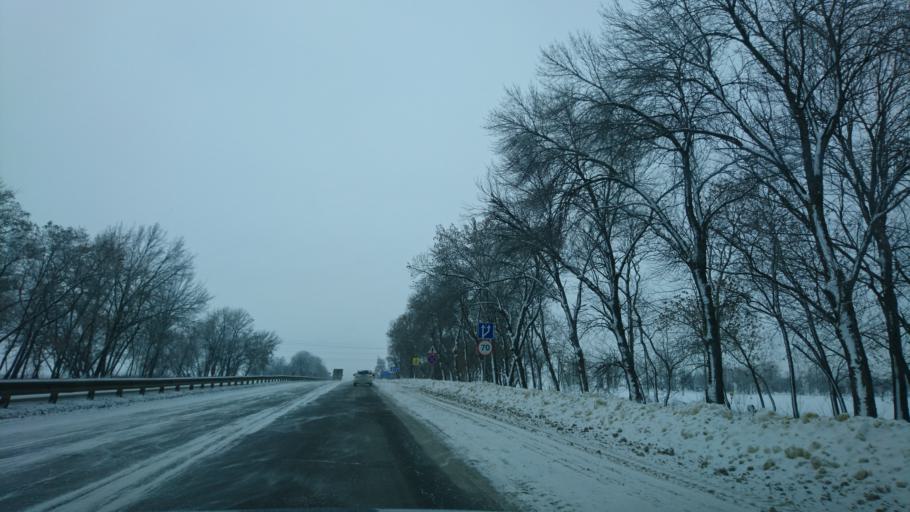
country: RU
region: Belgorod
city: Mayskiy
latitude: 50.4388
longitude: 36.3923
